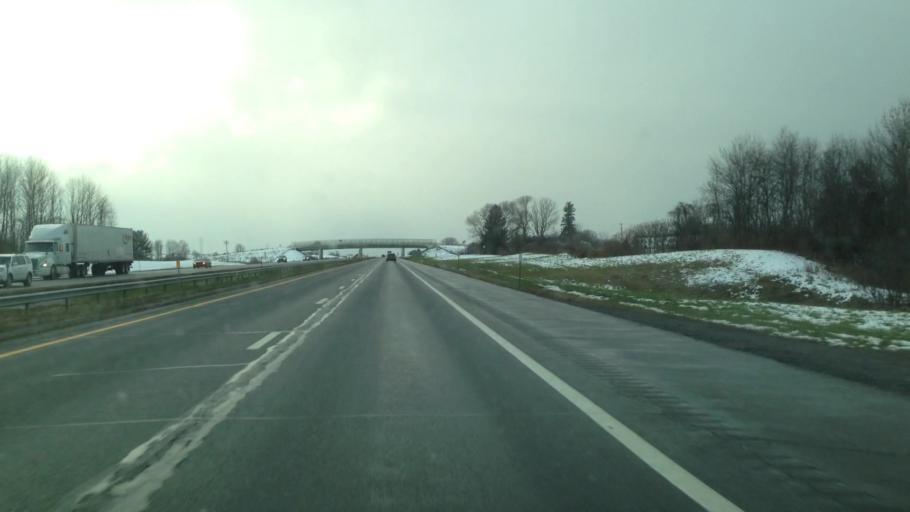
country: US
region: New York
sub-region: Montgomery County
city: Amsterdam
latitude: 42.9281
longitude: -74.2205
